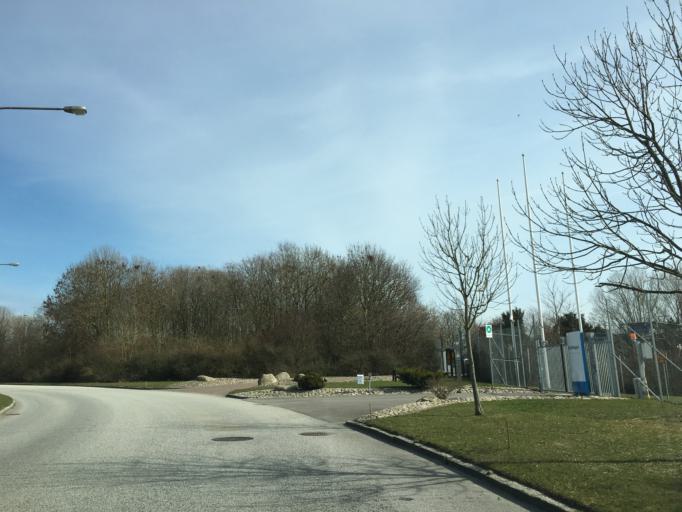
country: SE
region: Skane
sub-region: Lunds Kommun
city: Lund
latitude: 55.7215
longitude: 13.1570
